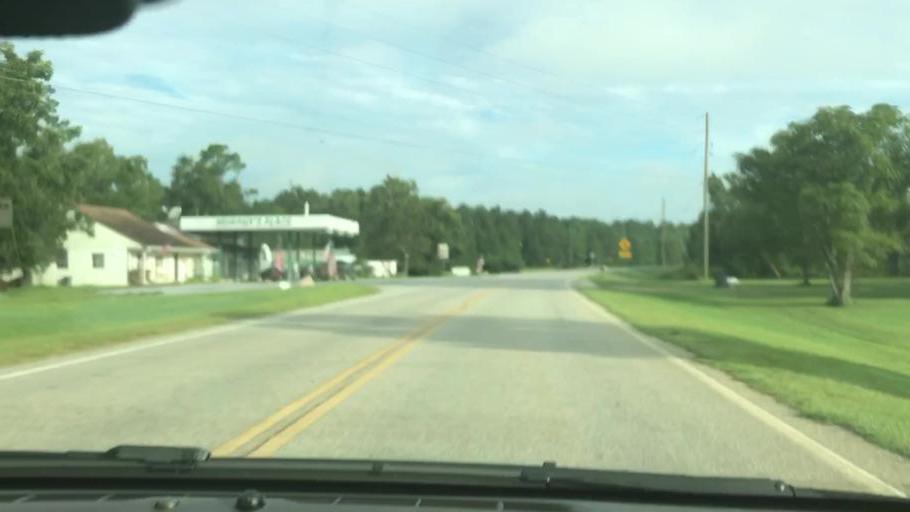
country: US
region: Georgia
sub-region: Quitman County
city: Georgetown
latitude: 31.7691
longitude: -85.0908
